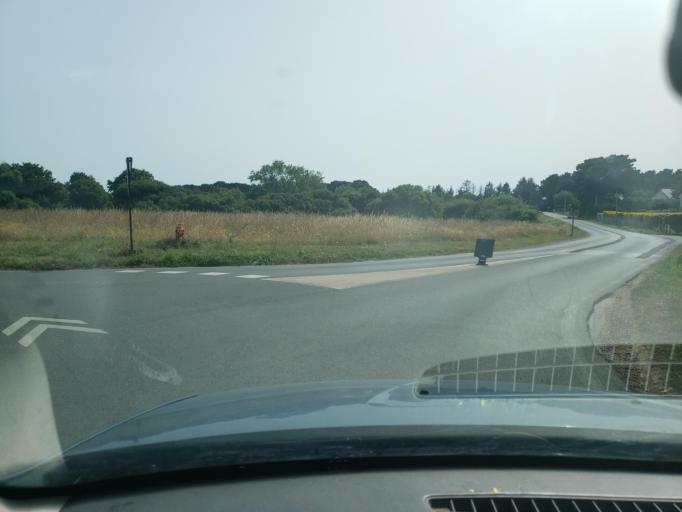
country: FR
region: Brittany
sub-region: Departement du Finistere
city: Plobannalec-Lesconil
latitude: 47.8019
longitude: -4.2293
